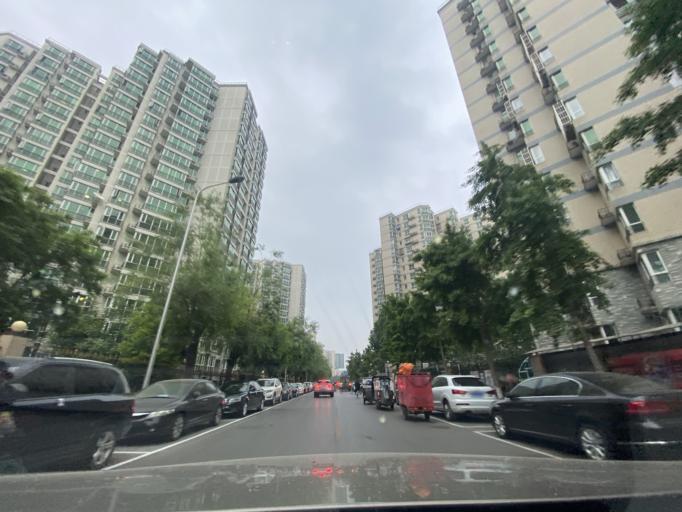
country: CN
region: Beijing
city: Sijiqing
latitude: 39.9582
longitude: 116.2754
